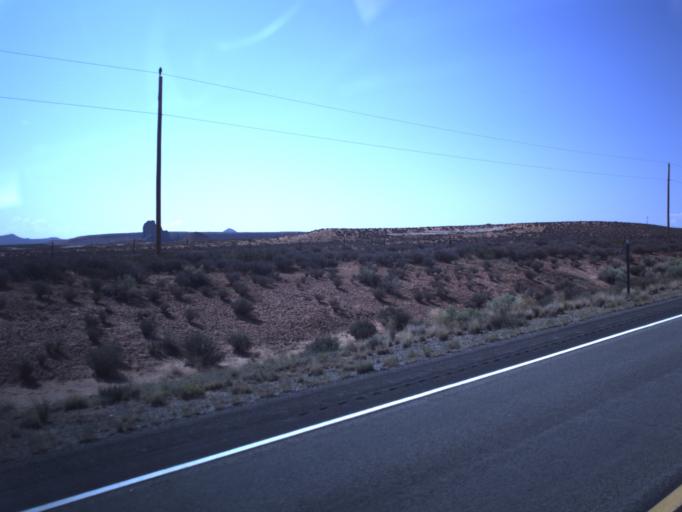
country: US
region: Utah
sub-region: San Juan County
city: Blanding
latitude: 37.0588
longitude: -109.5645
